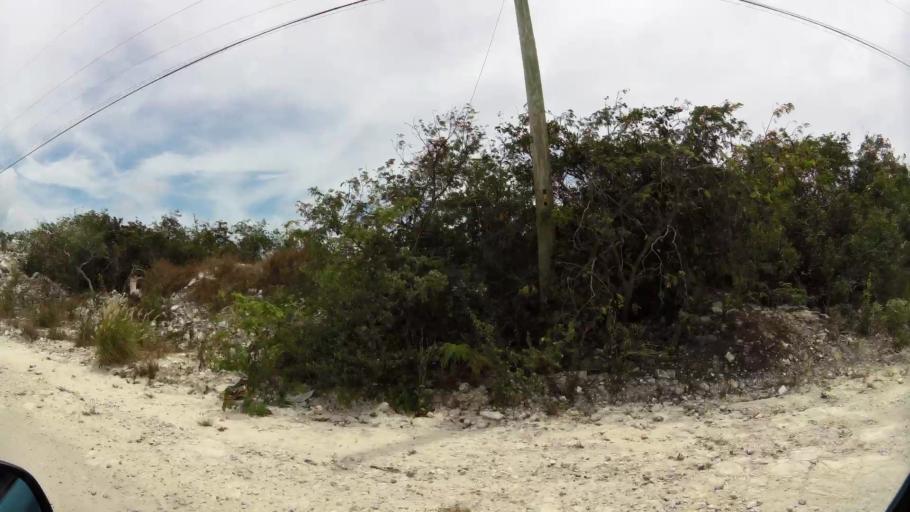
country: BS
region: Mayaguana
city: Abraham's Bay
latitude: 21.8080
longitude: -72.2953
